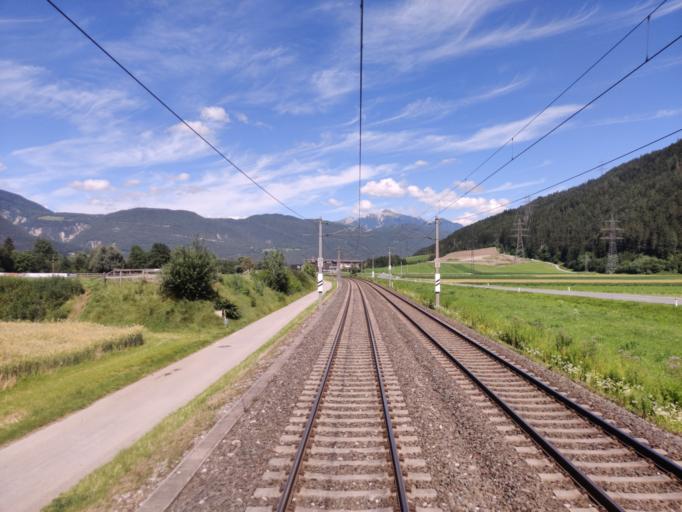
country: AT
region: Tyrol
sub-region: Politischer Bezirk Imst
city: Rietz
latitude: 47.2942
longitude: 11.0514
